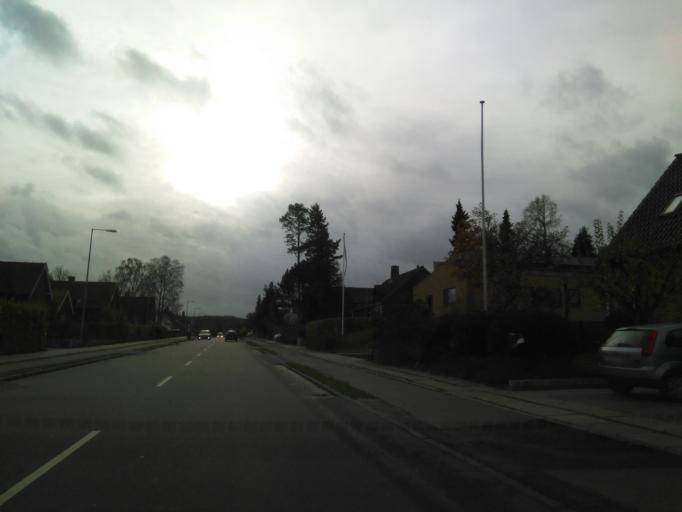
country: DK
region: Central Jutland
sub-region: Arhus Kommune
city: Arhus
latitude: 56.1901
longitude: 10.2283
